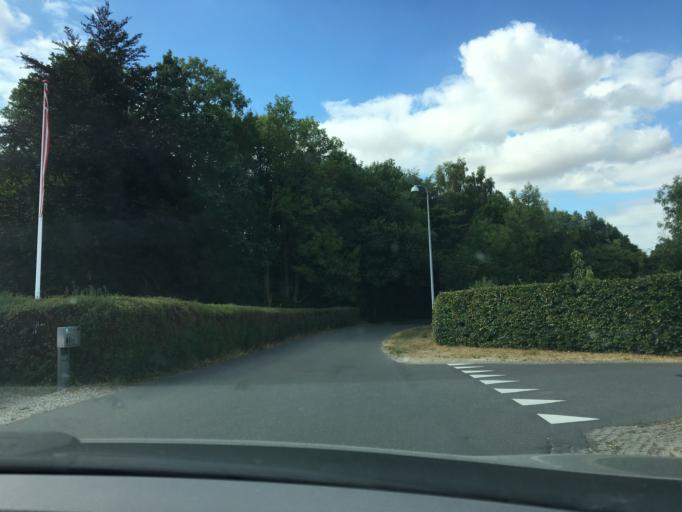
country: DK
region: South Denmark
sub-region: Assens Kommune
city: Vissenbjerg
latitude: 55.4504
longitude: 10.1822
